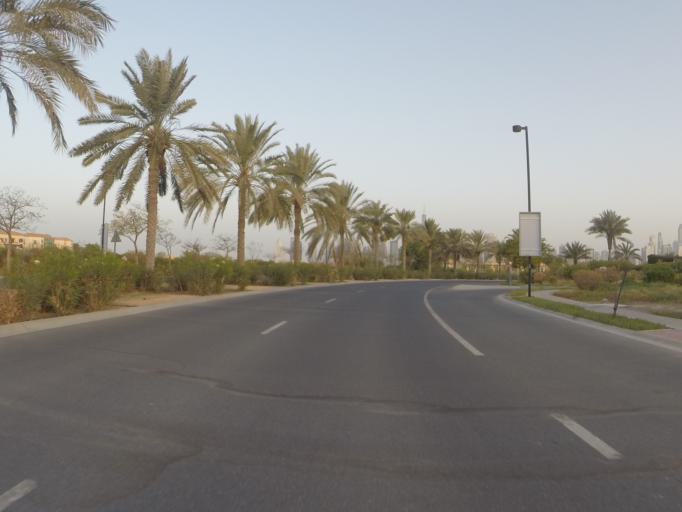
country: AE
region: Dubai
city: Dubai
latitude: 25.0548
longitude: 55.1605
